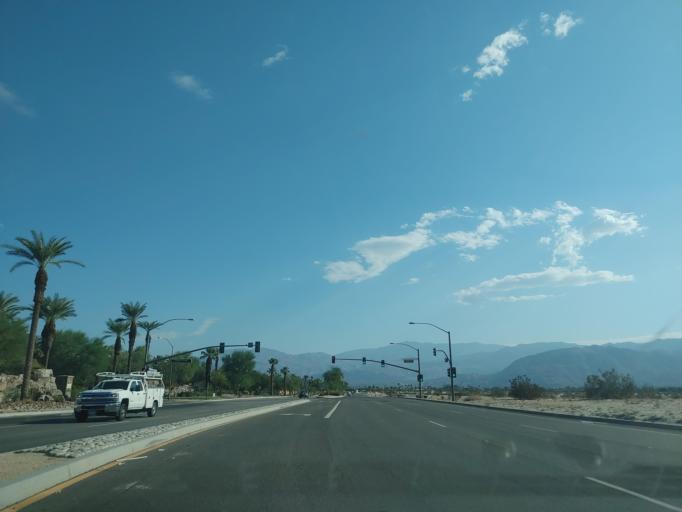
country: US
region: California
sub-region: Riverside County
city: Thousand Palms
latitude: 33.7835
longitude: -116.3882
